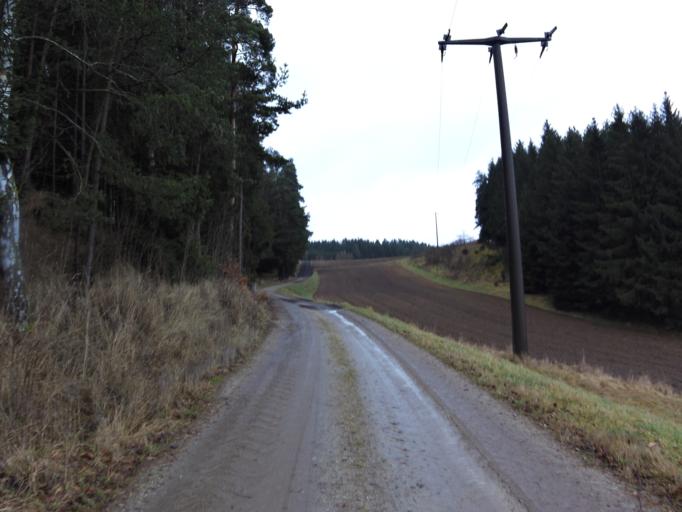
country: DE
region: Bavaria
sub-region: Upper Franconia
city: Wunsiedel
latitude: 50.0662
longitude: 12.0296
